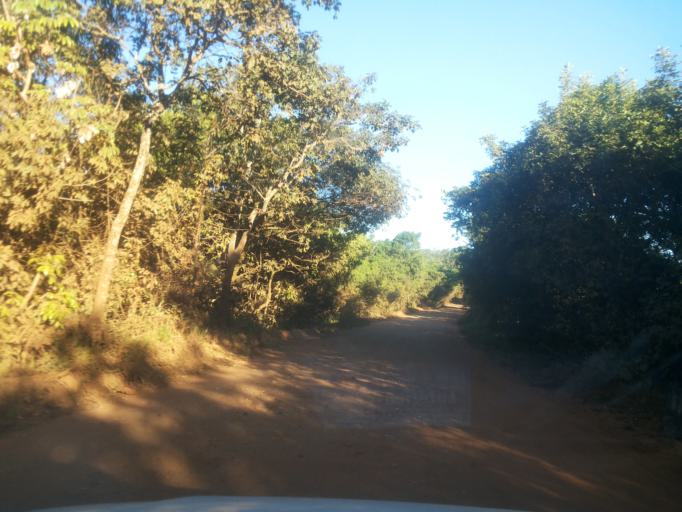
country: BR
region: Minas Gerais
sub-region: Campina Verde
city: Campina Verde
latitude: -19.3274
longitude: -49.7944
